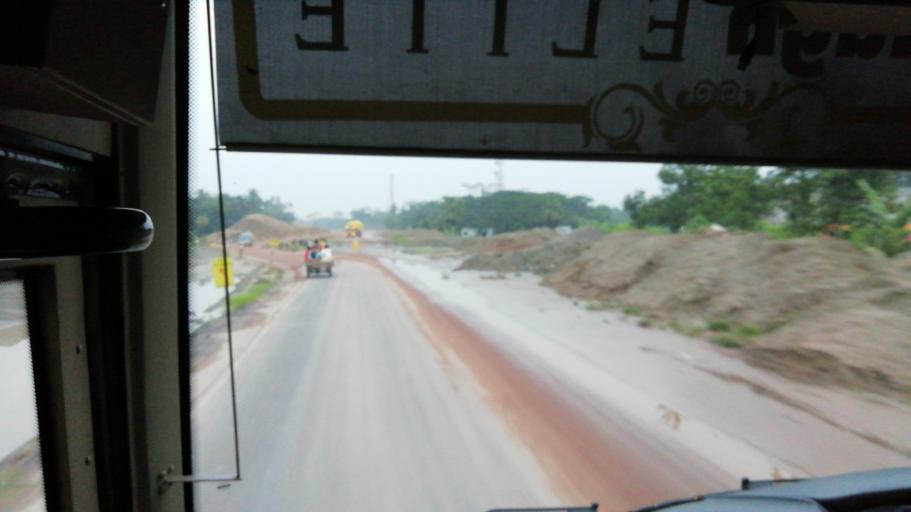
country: BD
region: Dhaka
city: Char Bhadrasan
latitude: 23.4018
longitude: 90.1410
